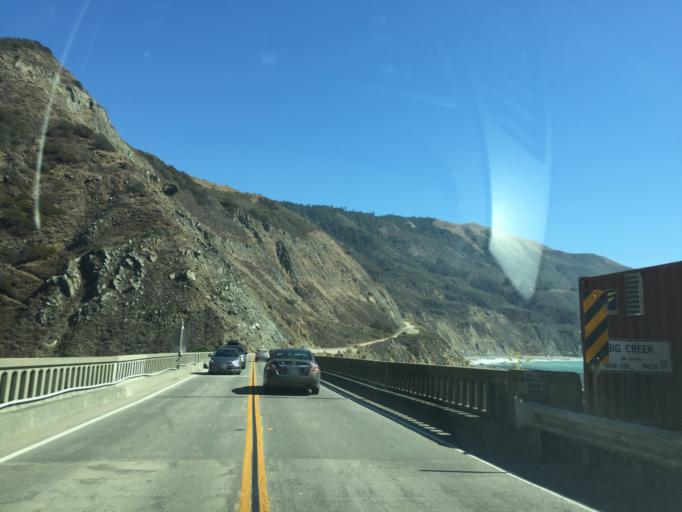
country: US
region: California
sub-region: Monterey County
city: Greenfield
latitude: 36.0703
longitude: -121.6011
